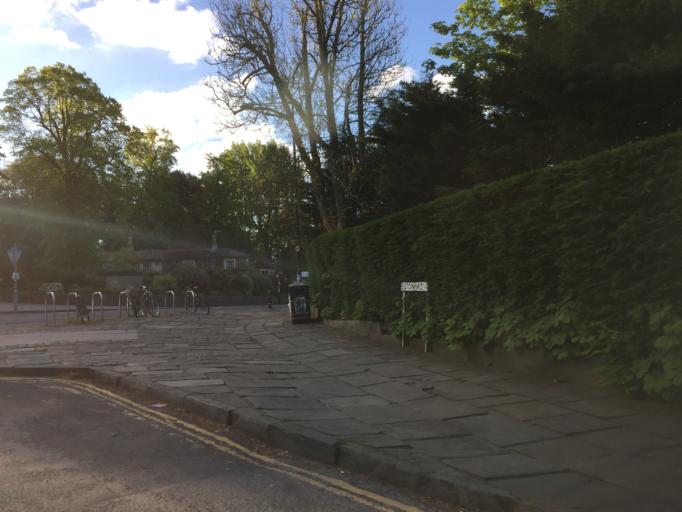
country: GB
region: England
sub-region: Bristol
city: Bristol
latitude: 51.4586
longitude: -2.6040
